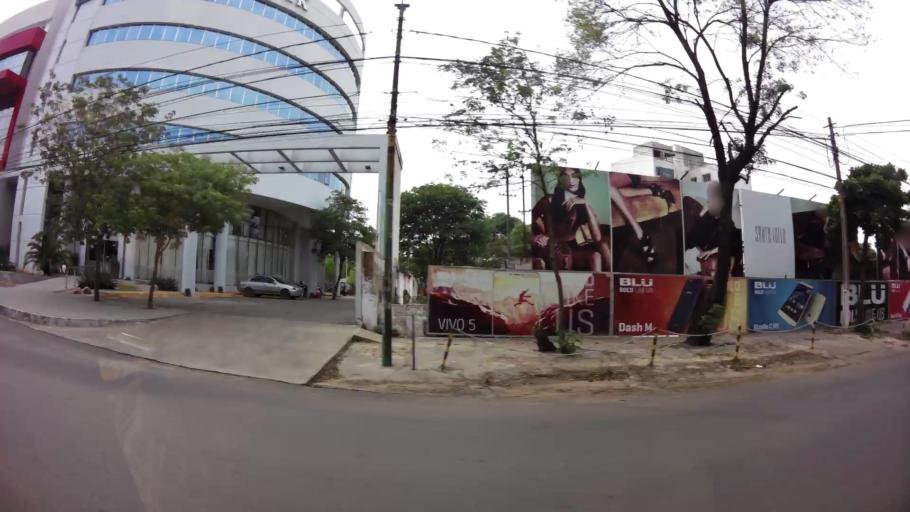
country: PY
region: Central
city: Fernando de la Mora
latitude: -25.2799
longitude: -57.5582
